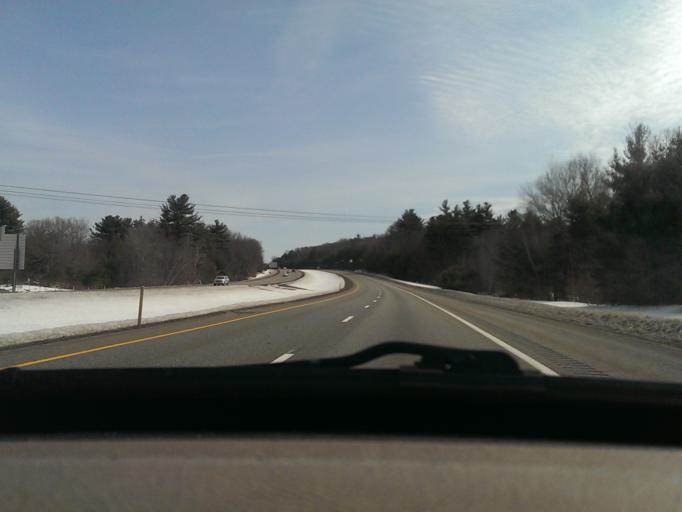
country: US
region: Massachusetts
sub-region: Worcester County
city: Millville
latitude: 42.0335
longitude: -71.6201
